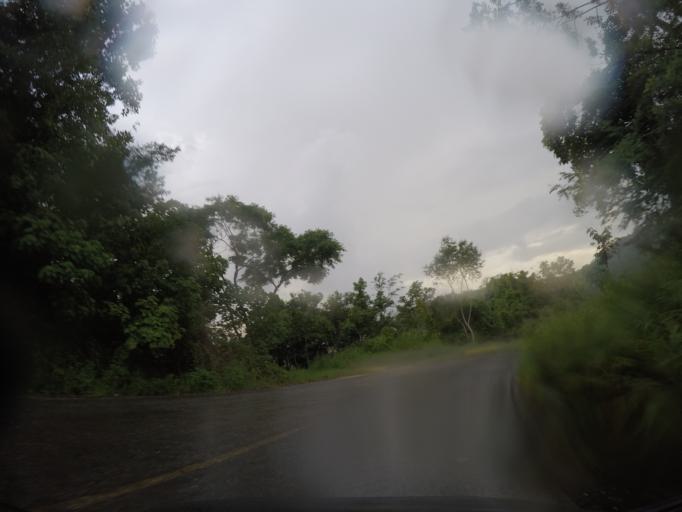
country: MX
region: Oaxaca
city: San Gabriel Mixtepec
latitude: 16.0582
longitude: -97.0747
